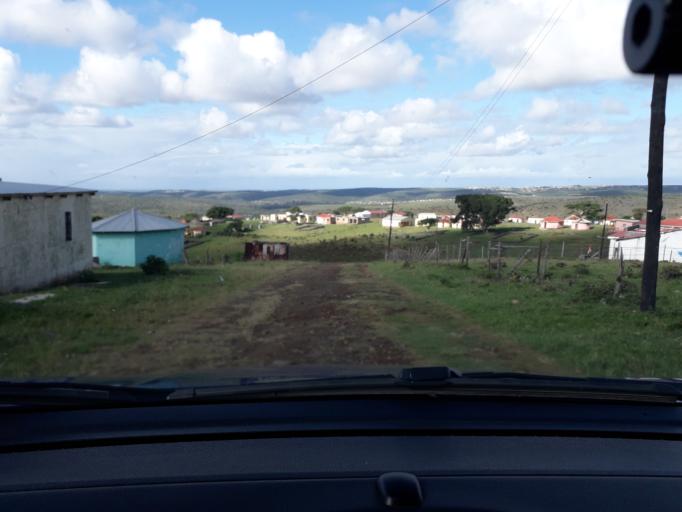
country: ZA
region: Eastern Cape
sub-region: Buffalo City Metropolitan Municipality
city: Bhisho
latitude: -33.1113
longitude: 27.4265
